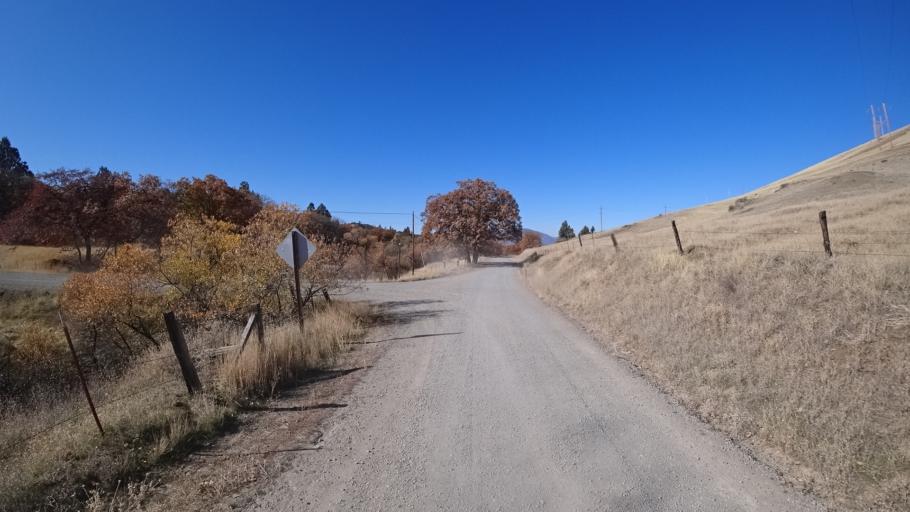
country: US
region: California
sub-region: Siskiyou County
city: Montague
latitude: 41.7933
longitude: -122.3605
